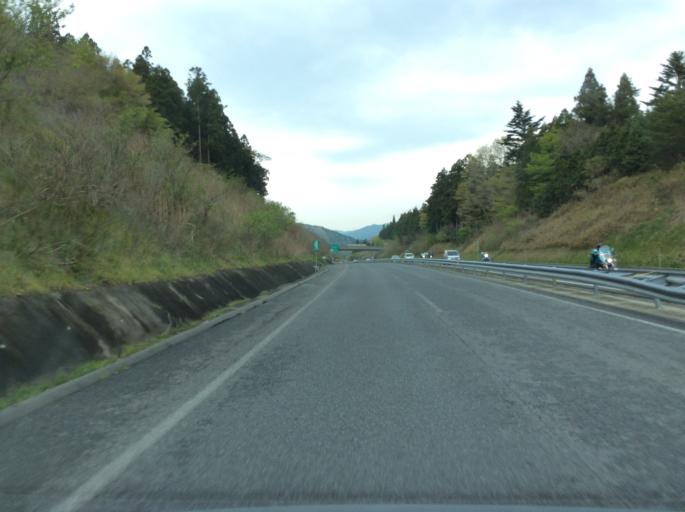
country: JP
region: Fukushima
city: Iwaki
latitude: 37.0934
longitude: 140.7841
